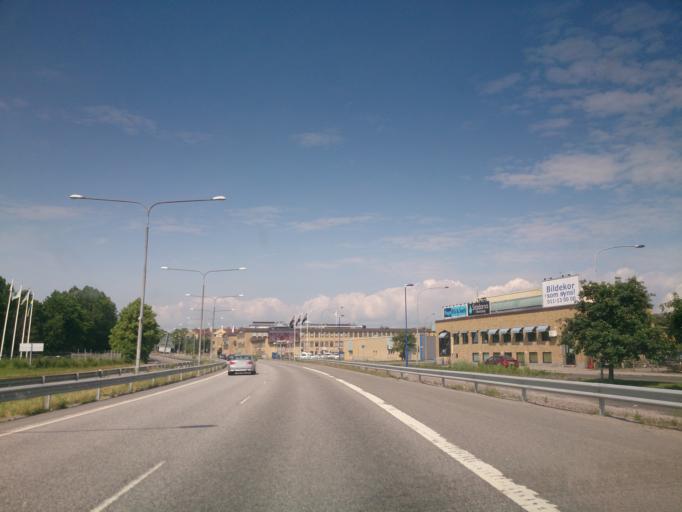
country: SE
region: OEstergoetland
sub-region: Norrkopings Kommun
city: Norrkoping
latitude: 58.5832
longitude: 16.2086
